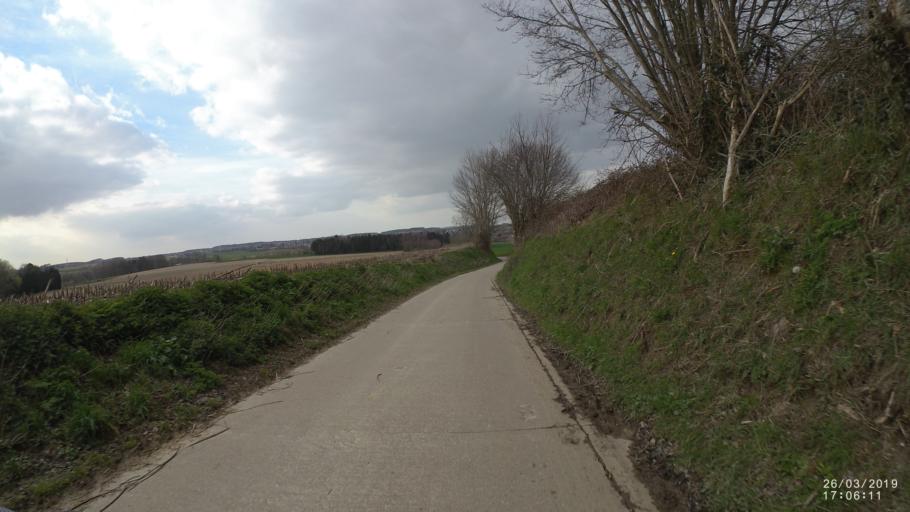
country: BE
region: Flanders
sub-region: Provincie Vlaams-Brabant
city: Huldenberg
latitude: 50.8337
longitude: 4.5830
